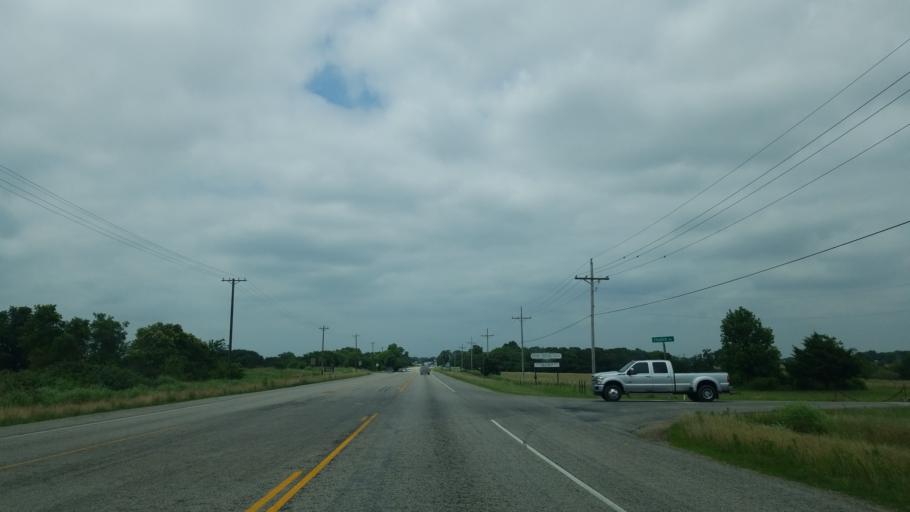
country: US
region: Texas
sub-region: Denton County
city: Pilot Point
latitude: 33.3710
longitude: -96.9638
